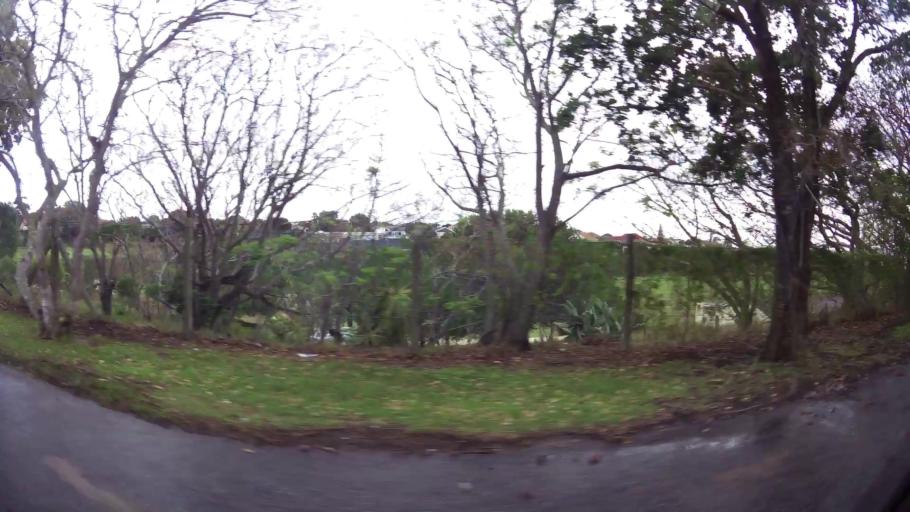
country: ZA
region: Eastern Cape
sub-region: Nelson Mandela Bay Metropolitan Municipality
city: Port Elizabeth
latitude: -33.9499
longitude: 25.5945
